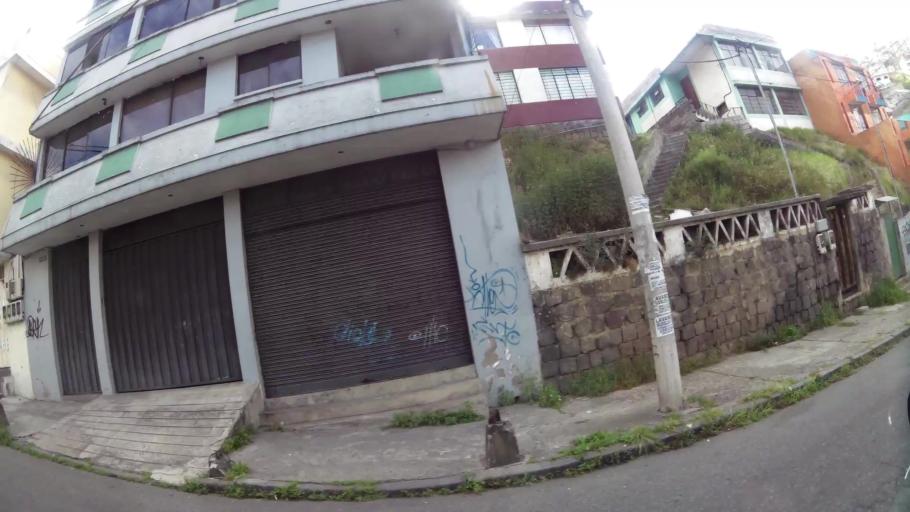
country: EC
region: Pichincha
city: Quito
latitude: -0.2291
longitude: -78.5017
